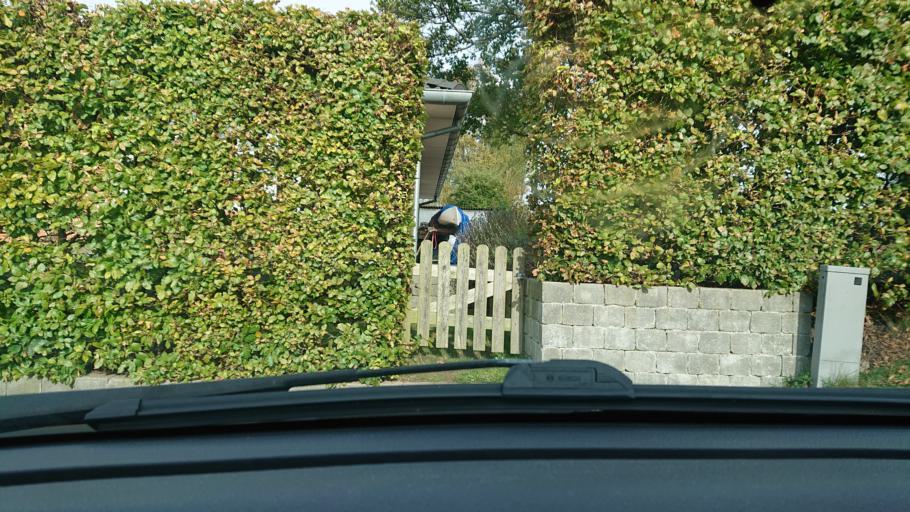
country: DK
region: South Denmark
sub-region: Nyborg Kommune
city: Nyborg
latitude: 55.3065
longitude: 10.7647
